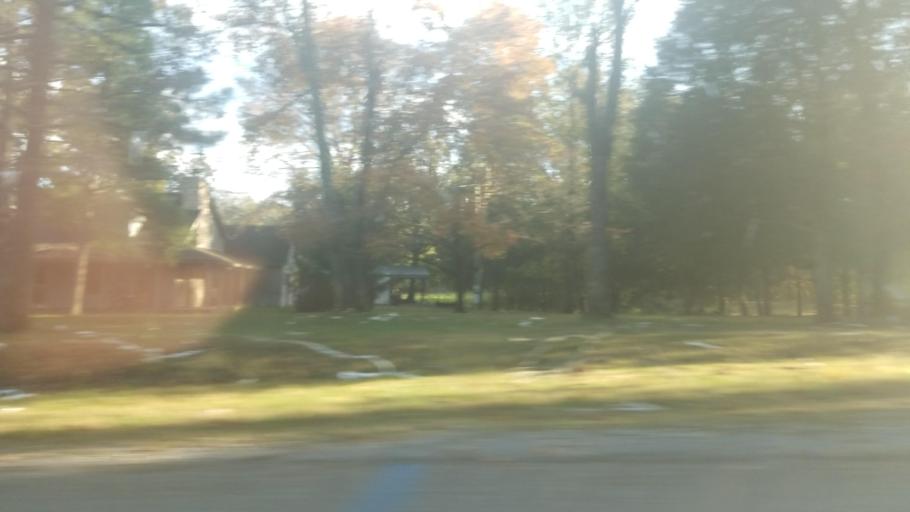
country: US
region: Illinois
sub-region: Williamson County
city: Marion
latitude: 37.7602
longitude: -88.7845
